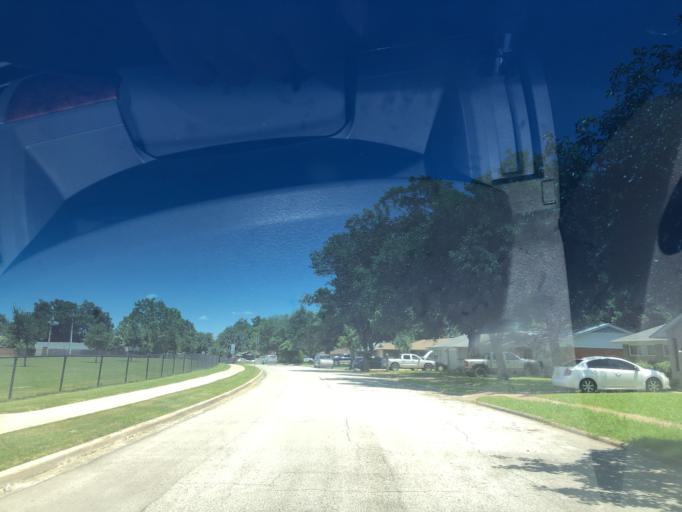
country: US
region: Texas
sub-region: Dallas County
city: Grand Prairie
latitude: 32.7168
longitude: -97.0124
